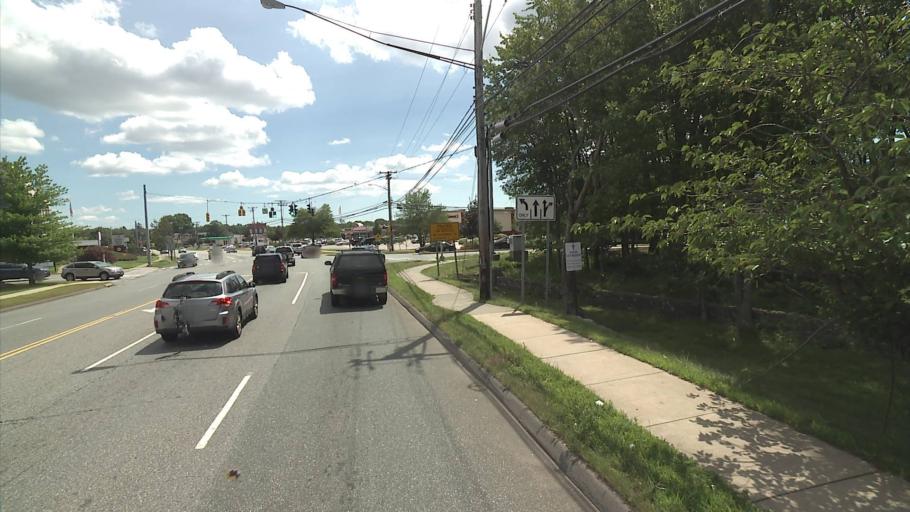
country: US
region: Connecticut
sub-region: New London County
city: Long Hill
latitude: 41.3471
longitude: -72.0523
